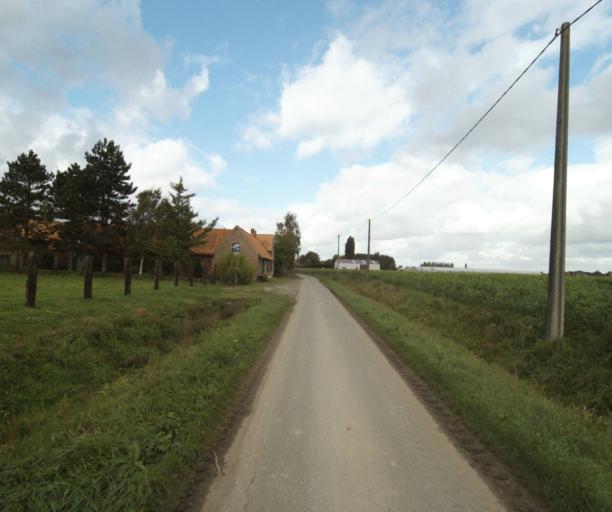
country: FR
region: Nord-Pas-de-Calais
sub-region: Departement du Nord
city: Perenchies
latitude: 50.6961
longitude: 2.9597
